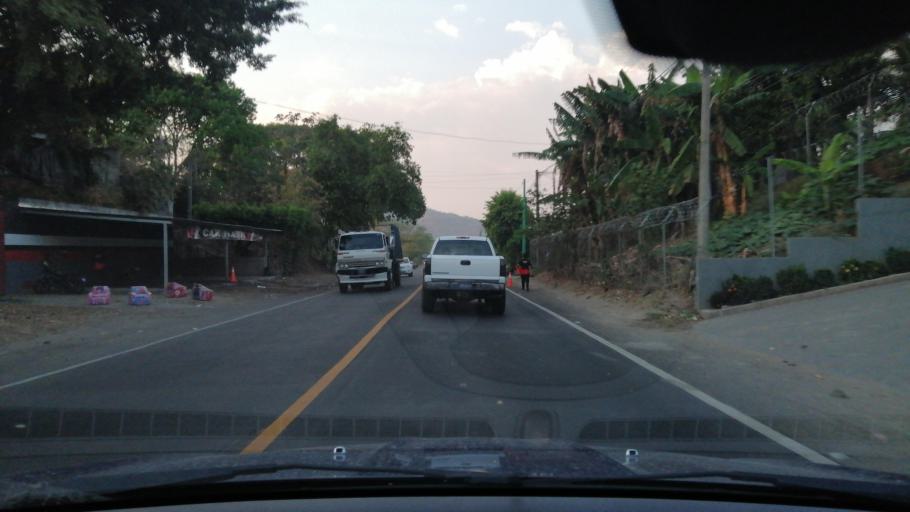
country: SV
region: Santa Ana
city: Santa Ana
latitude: 14.0016
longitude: -89.5417
